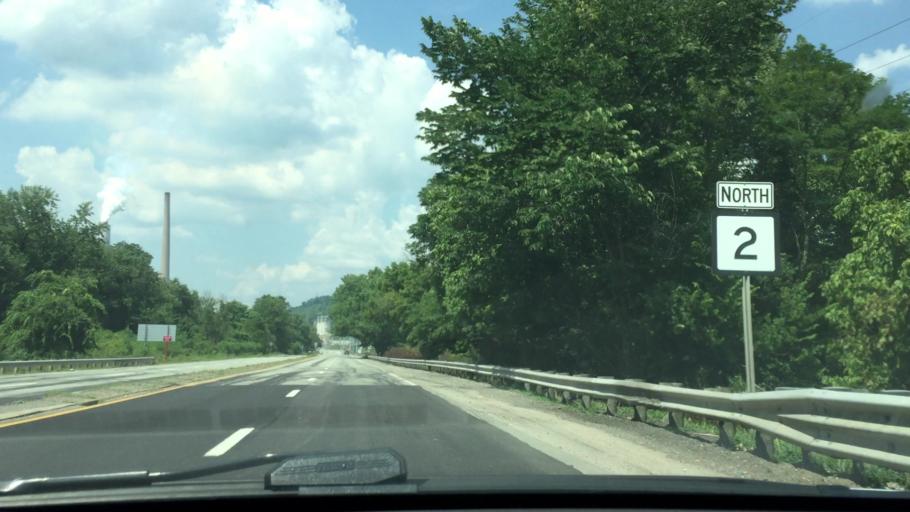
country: US
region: Ohio
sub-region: Belmont County
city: Powhatan Point
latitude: 39.8097
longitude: -80.8156
